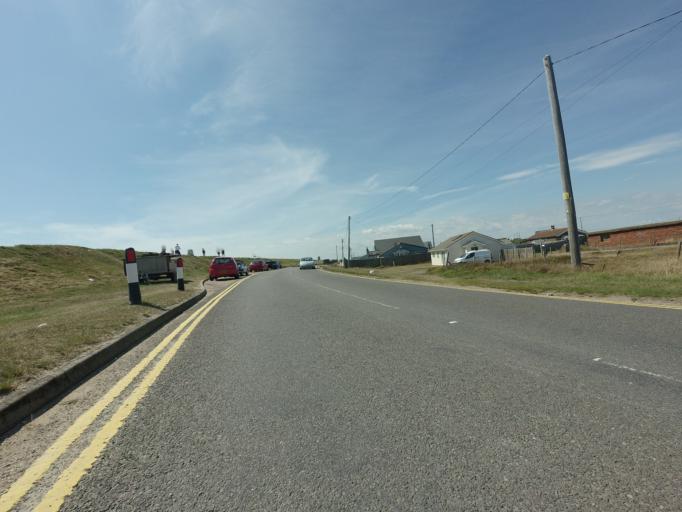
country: GB
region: England
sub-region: Kent
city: Lydd
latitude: 50.9276
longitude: 0.8305
